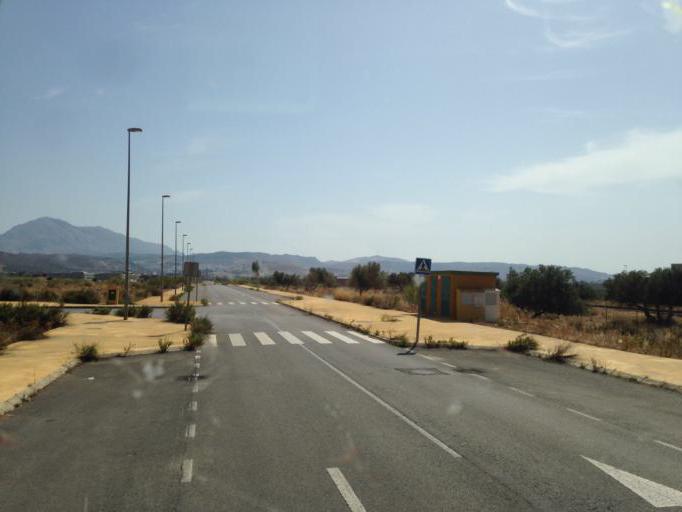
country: ES
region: Andalusia
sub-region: Provincia de Malaga
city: Antequera
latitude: 37.0454
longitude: -4.5141
